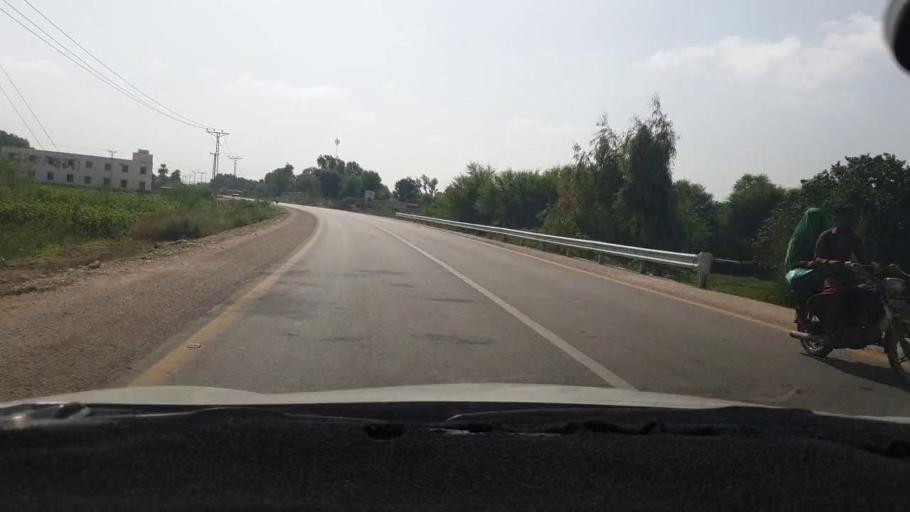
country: PK
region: Sindh
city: Mirpur Khas
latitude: 25.7239
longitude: 69.1126
